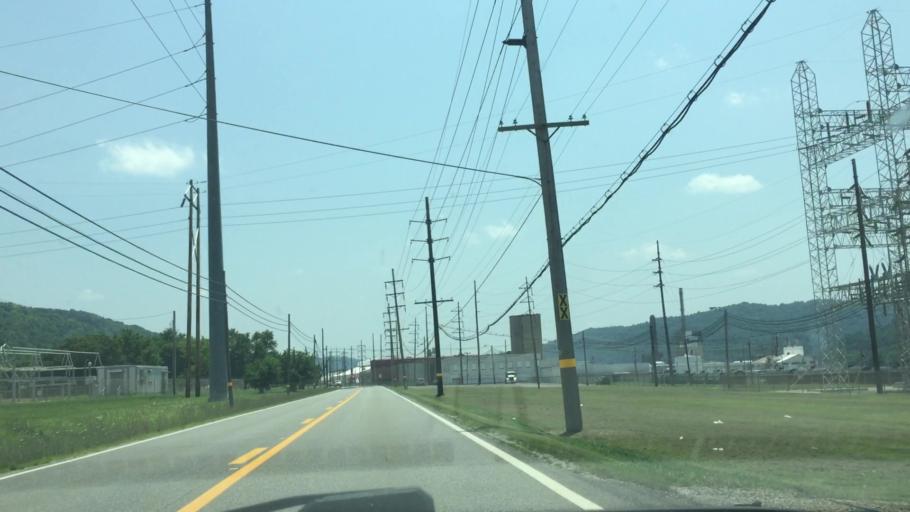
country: US
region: West Virginia
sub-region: Wetzel County
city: New Martinsville
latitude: 39.7549
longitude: -80.8566
